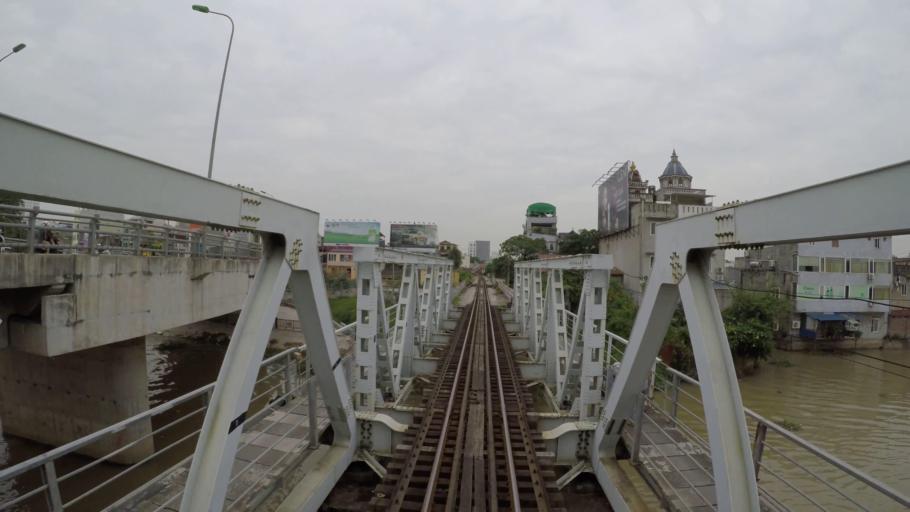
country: VN
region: Hai Phong
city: Haiphong
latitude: 20.8709
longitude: 106.6517
